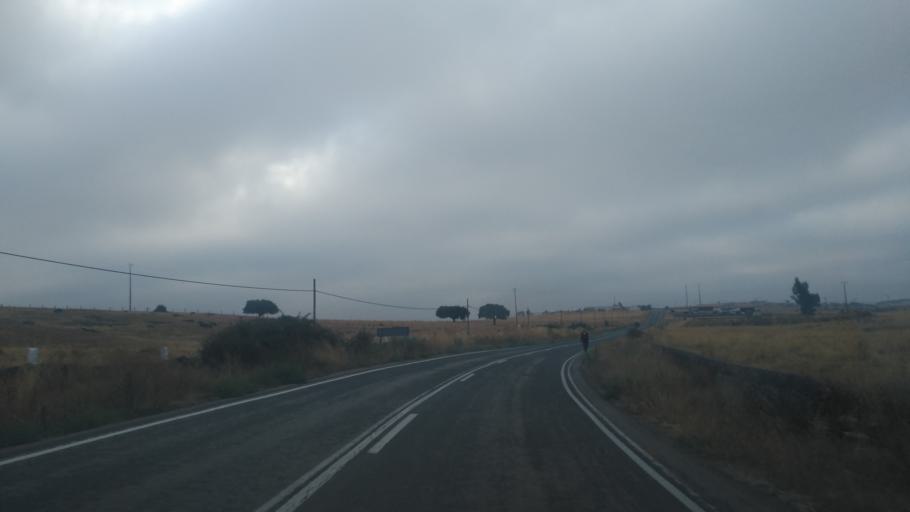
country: ES
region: Castille and Leon
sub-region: Provincia de Salamanca
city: Vecinos
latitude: 40.7857
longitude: -5.8873
